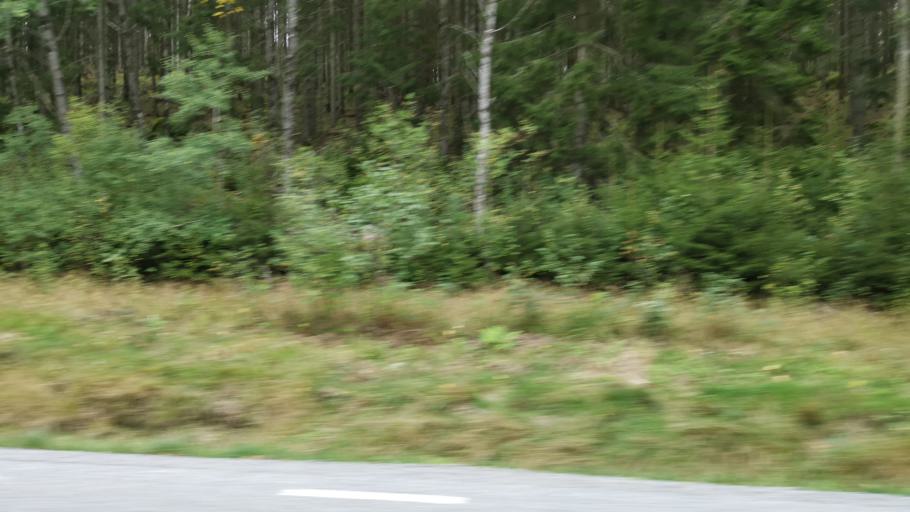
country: SE
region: Vaestra Goetaland
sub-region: Tanums Kommun
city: Tanumshede
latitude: 58.7038
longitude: 11.3375
